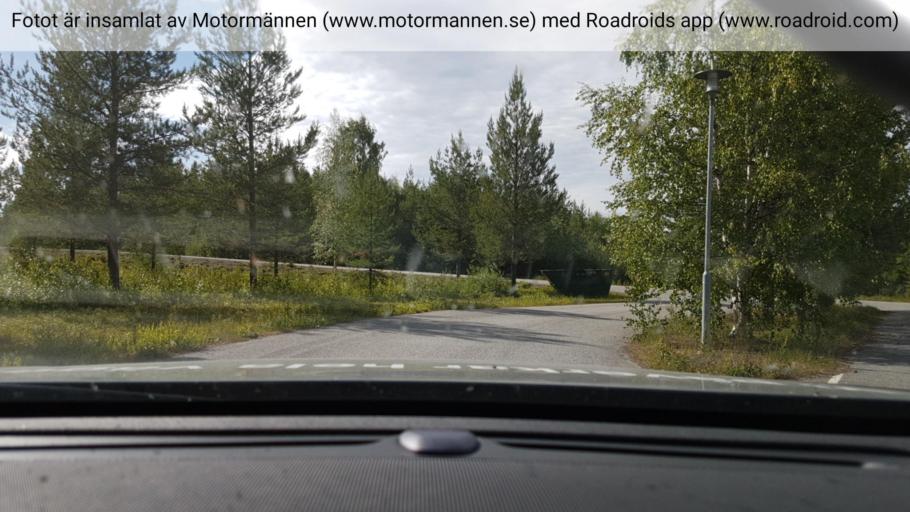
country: SE
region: Vaesterbotten
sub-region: Lycksele Kommun
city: Soderfors
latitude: 64.8299
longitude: 18.0329
